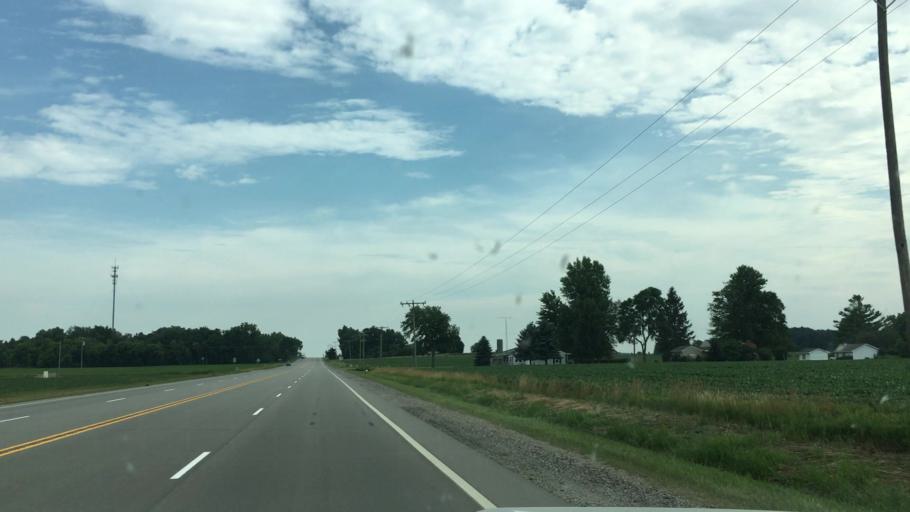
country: US
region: Michigan
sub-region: Sanilac County
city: Marlette
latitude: 43.3879
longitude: -83.0863
